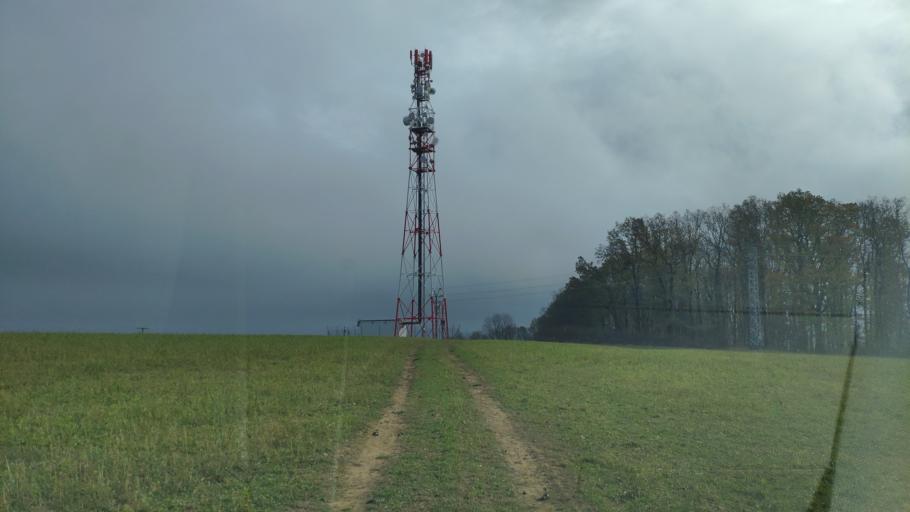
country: SK
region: Presovsky
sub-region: Okres Presov
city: Presov
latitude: 49.0046
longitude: 21.1992
